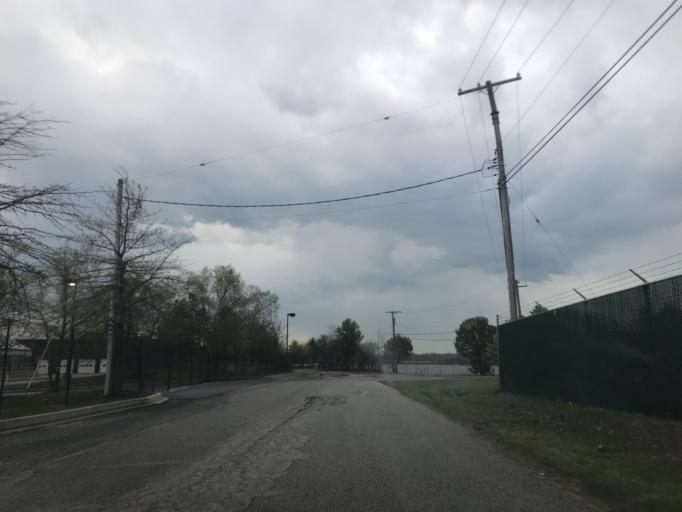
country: US
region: Maryland
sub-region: Anne Arundel County
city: Brooklyn Park
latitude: 39.2587
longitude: -76.6105
